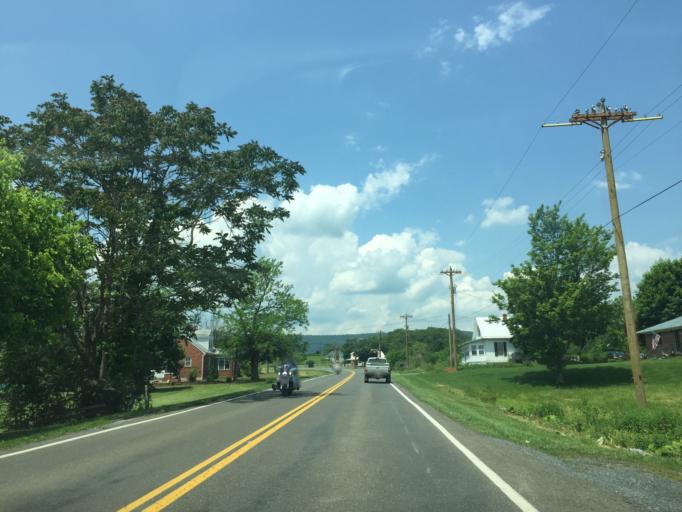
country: US
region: Virginia
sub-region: Shenandoah County
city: Strasburg
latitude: 39.0305
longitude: -78.3701
